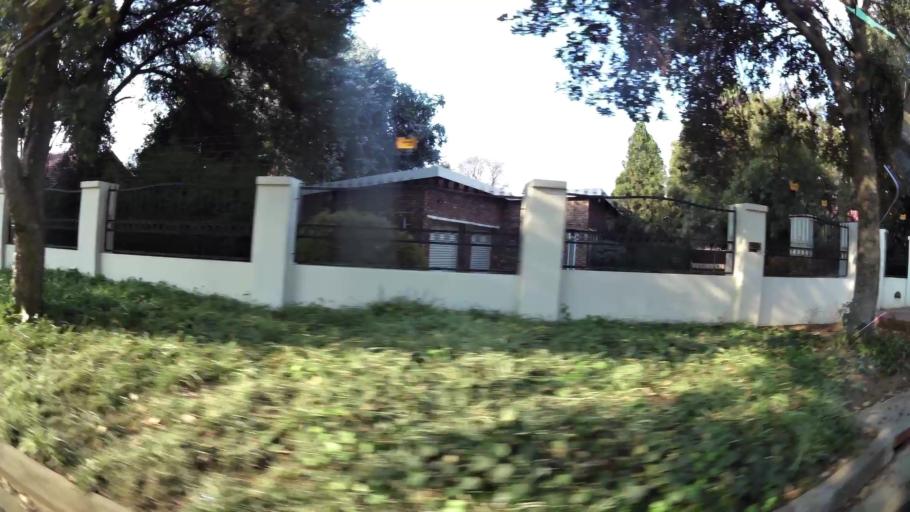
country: ZA
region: Gauteng
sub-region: Ekurhuleni Metropolitan Municipality
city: Benoni
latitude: -26.1081
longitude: 28.2890
